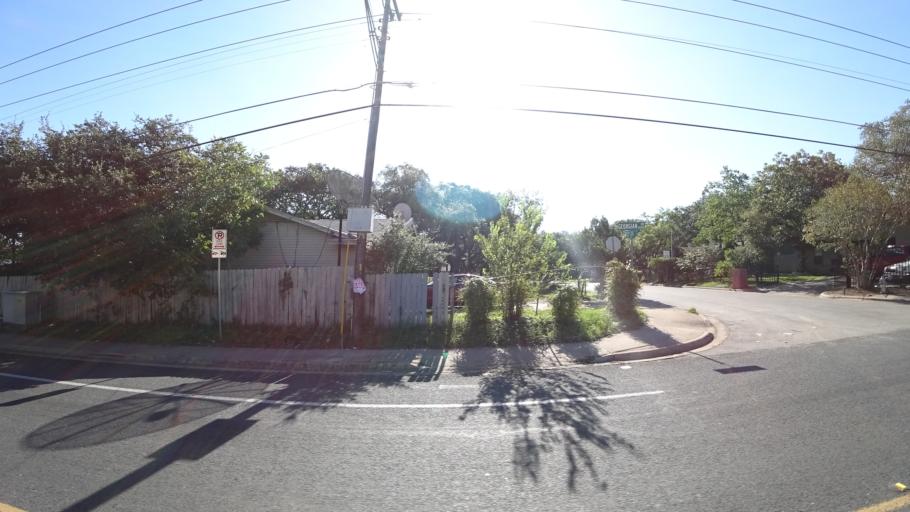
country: US
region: Texas
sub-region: Travis County
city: Austin
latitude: 30.3493
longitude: -97.7022
